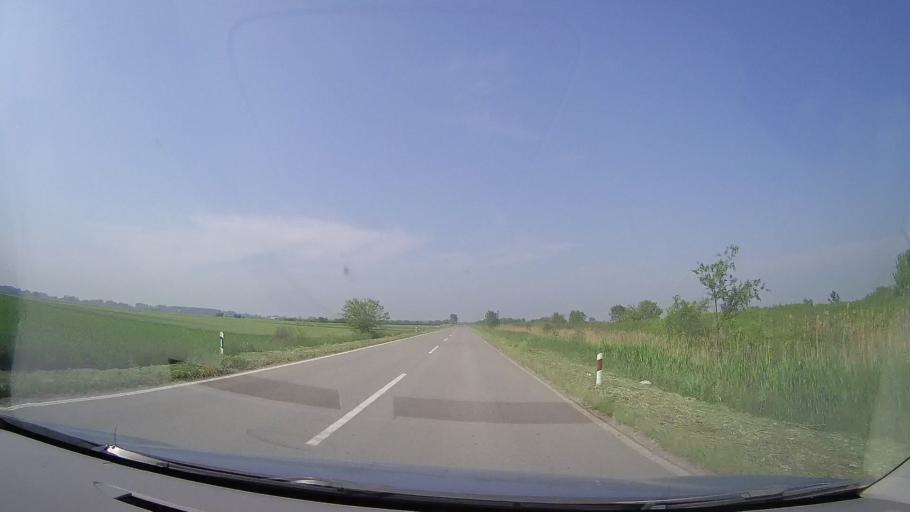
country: RS
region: Autonomna Pokrajina Vojvodina
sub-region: Srednjebanatski Okrug
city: Secanj
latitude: 45.3831
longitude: 20.7921
